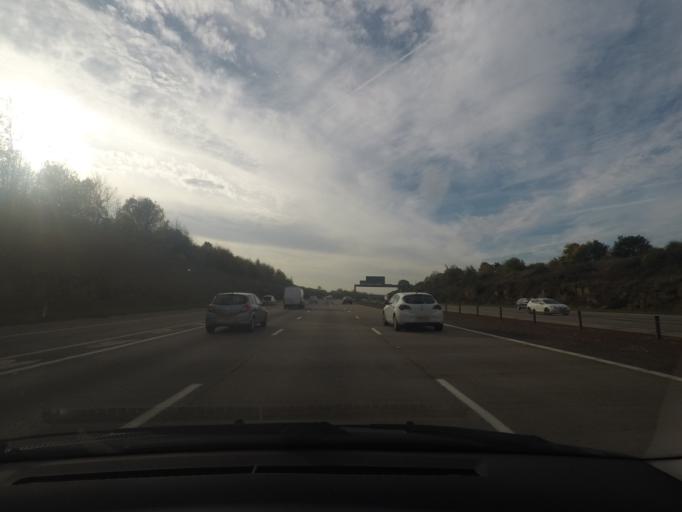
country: GB
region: England
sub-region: City and Borough of Leeds
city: Swillington
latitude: 53.7849
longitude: -1.4280
